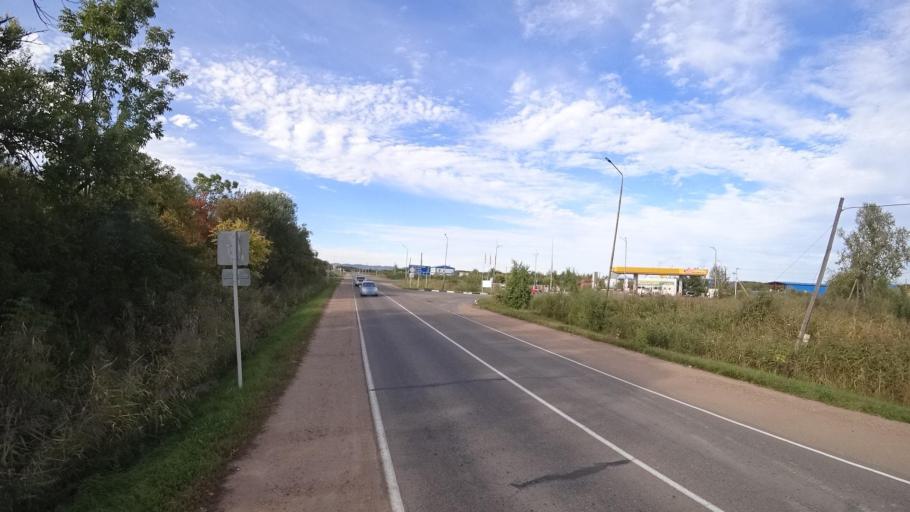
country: RU
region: Primorskiy
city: Dostoyevka
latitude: 44.2939
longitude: 133.4264
